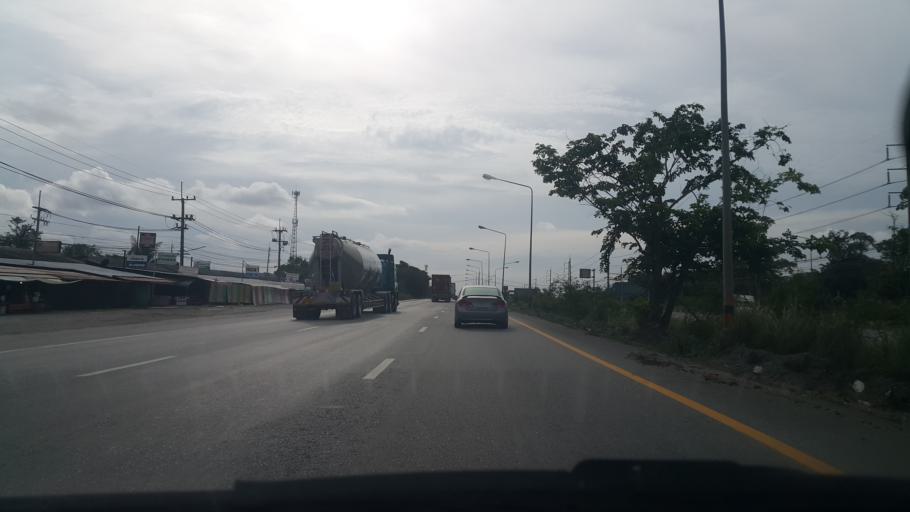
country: TH
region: Rayong
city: Nikhom Phattana
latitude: 12.8640
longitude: 101.0780
